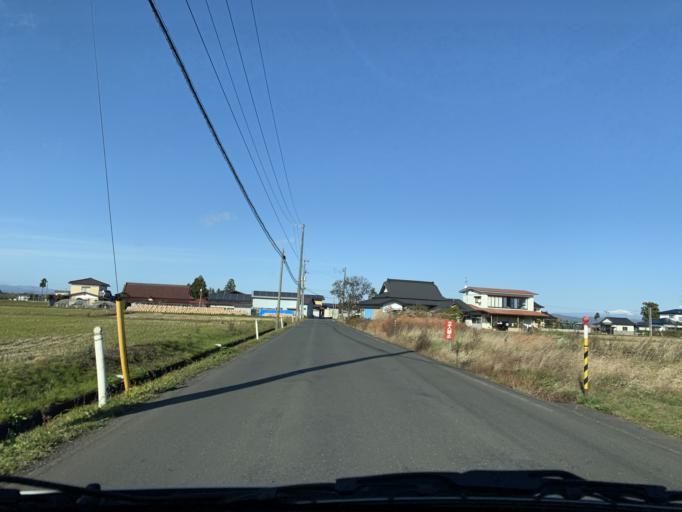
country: JP
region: Iwate
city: Mizusawa
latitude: 39.1574
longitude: 141.0977
